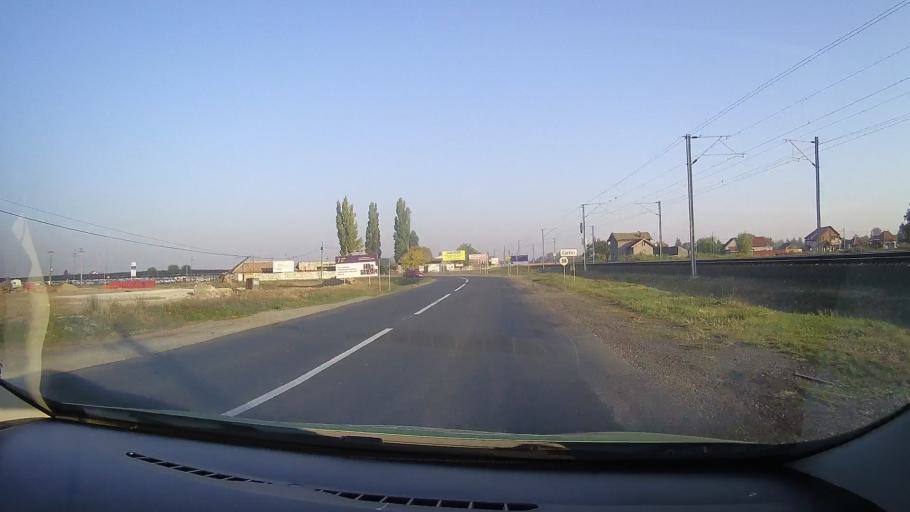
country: RO
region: Arad
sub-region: Comuna Curtici
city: Curtici
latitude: 46.3291
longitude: 21.3050
